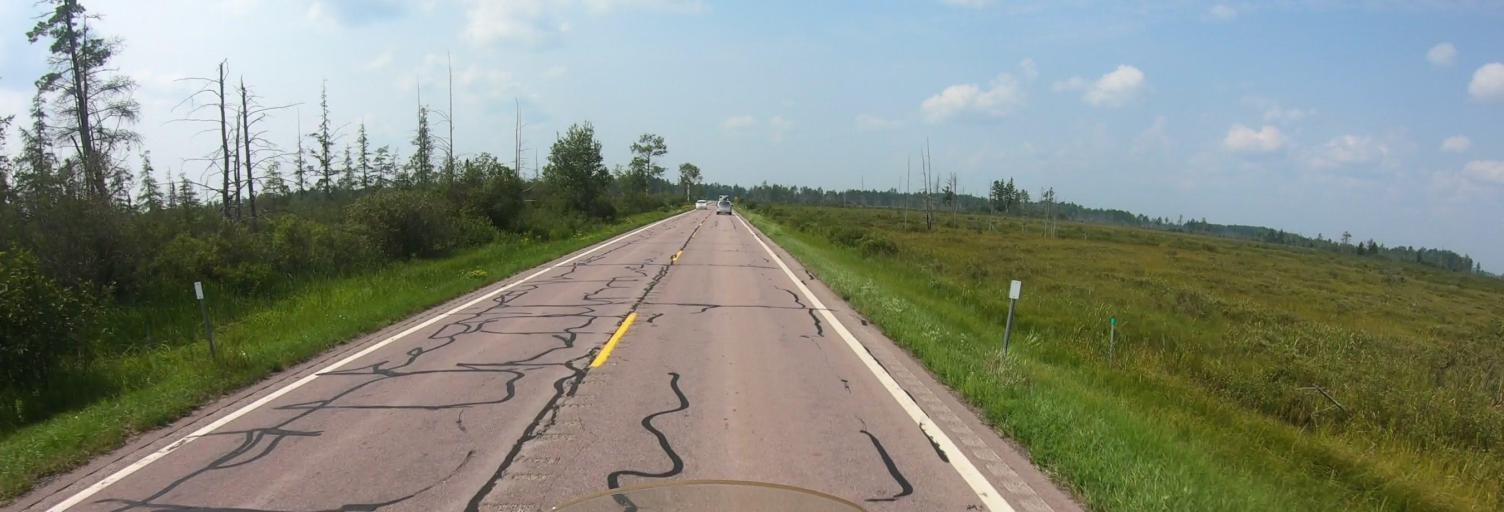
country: US
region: Michigan
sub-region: Luce County
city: Newberry
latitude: 46.4539
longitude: -85.4635
